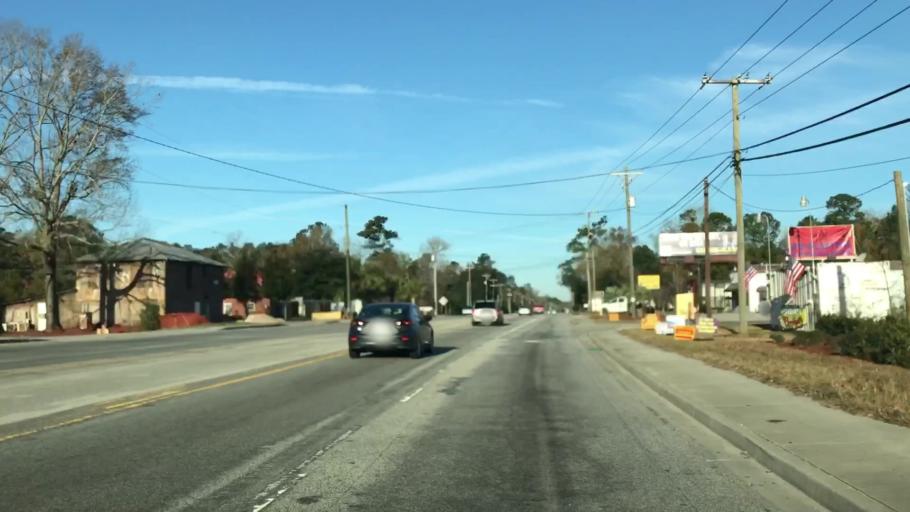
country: US
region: South Carolina
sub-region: Berkeley County
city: Ladson
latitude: 32.9822
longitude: -80.0885
